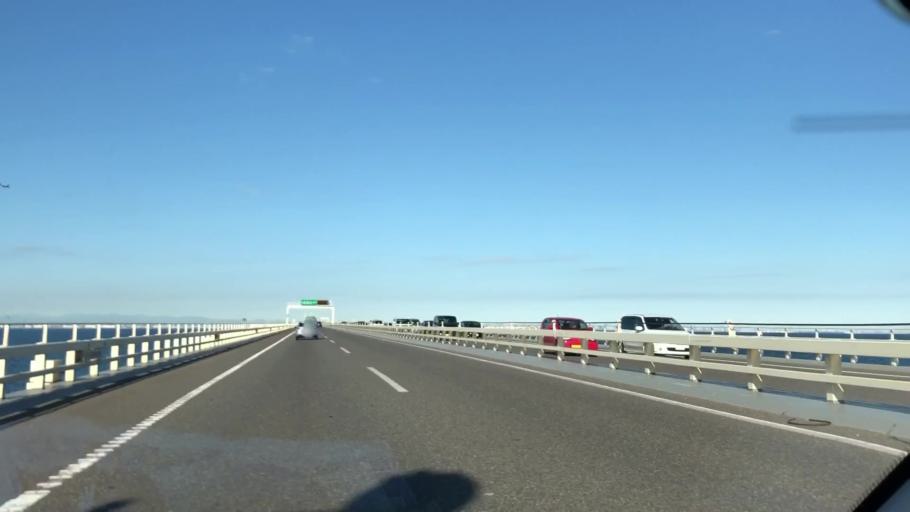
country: JP
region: Chiba
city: Kisarazu
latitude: 35.4421
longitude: 139.9069
